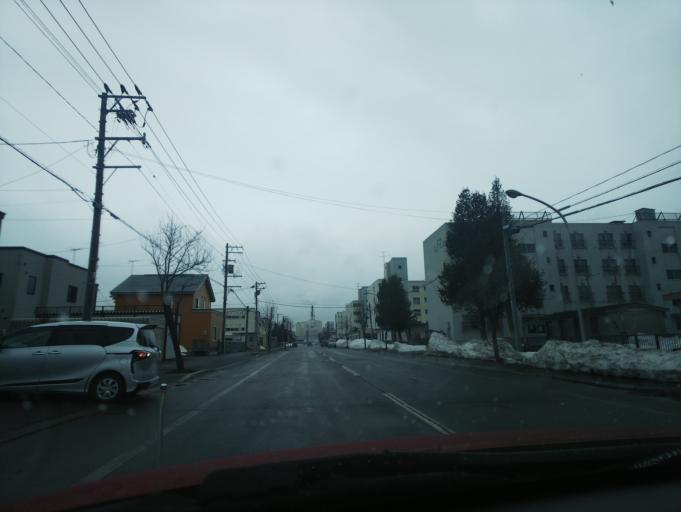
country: JP
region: Hokkaido
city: Nayoro
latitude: 44.3453
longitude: 142.4605
